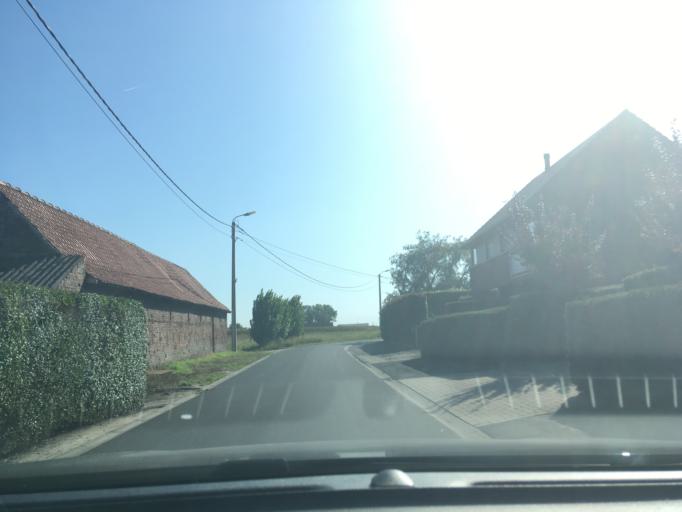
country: BE
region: Flanders
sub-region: Provincie West-Vlaanderen
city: Ledegem
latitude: 50.8695
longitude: 3.1412
